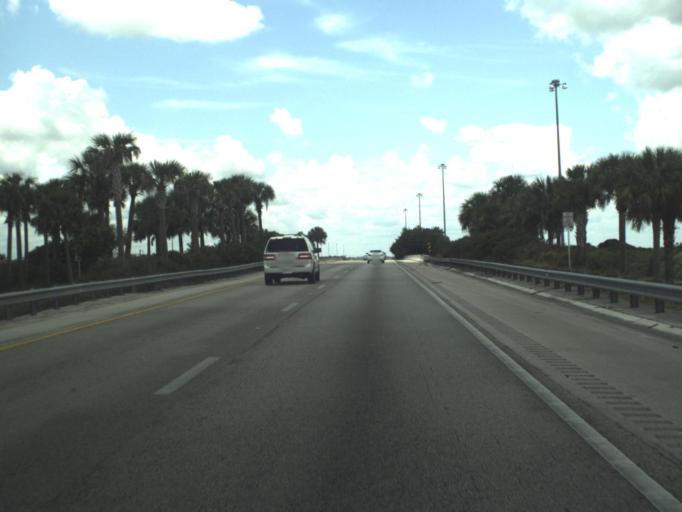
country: US
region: Florida
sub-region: Broward County
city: Weston
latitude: 26.1466
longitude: -80.6318
